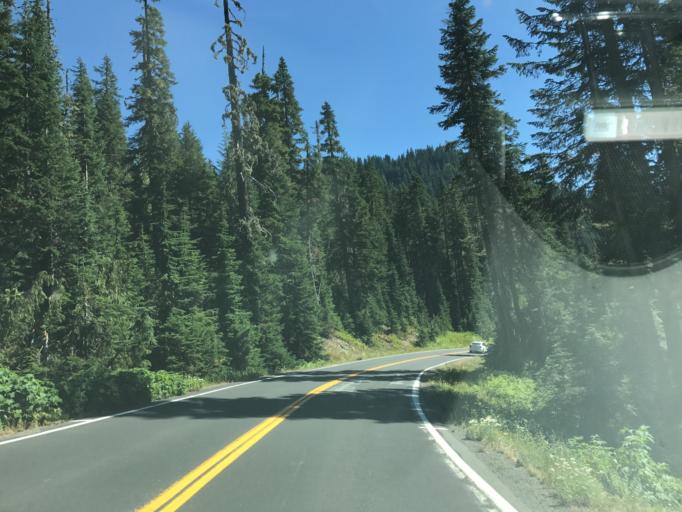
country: US
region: Washington
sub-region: King County
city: Enumclaw
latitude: 46.8657
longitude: -121.5341
